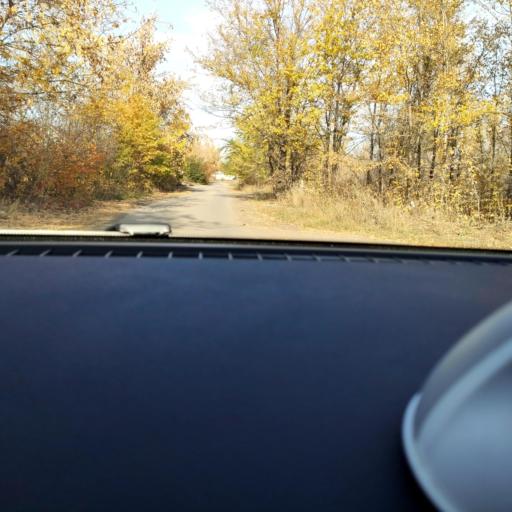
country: RU
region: Samara
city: Smyshlyayevka
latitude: 53.2423
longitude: 50.3607
